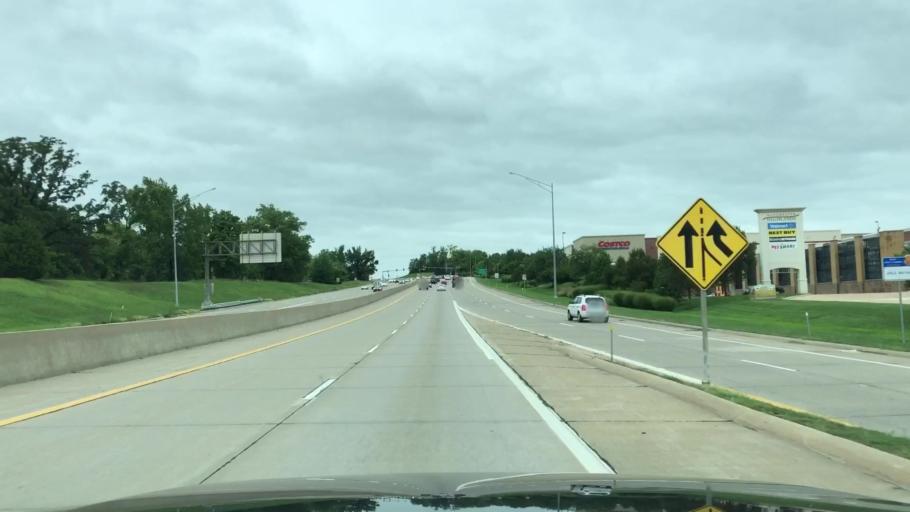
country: US
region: Missouri
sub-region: Saint Louis County
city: Manchester
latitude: 38.5948
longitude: -90.5086
